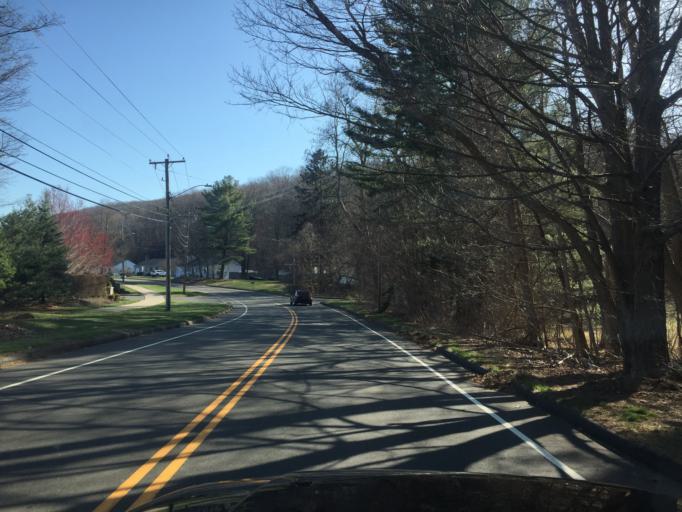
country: US
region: Connecticut
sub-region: Hartford County
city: Bristol
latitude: 41.6515
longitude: -72.9235
